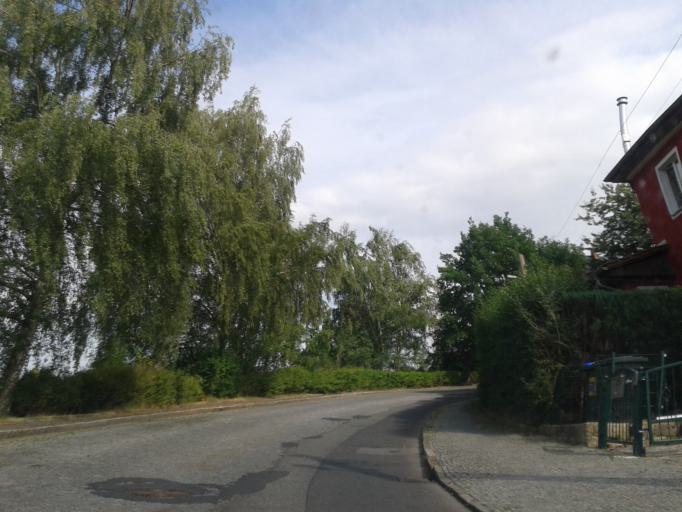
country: DE
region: Saxony
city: Bannewitz
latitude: 51.0148
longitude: 13.6898
